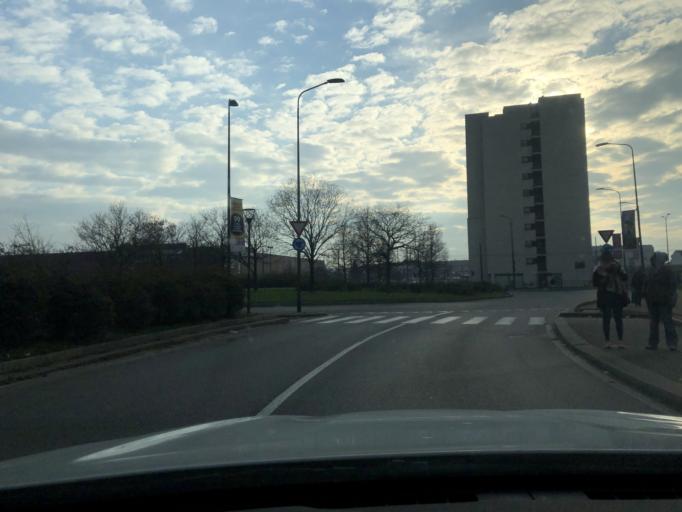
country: IT
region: Lombardy
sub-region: Citta metropolitana di Milano
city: Novate Milanese
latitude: 45.5086
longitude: 9.1381
